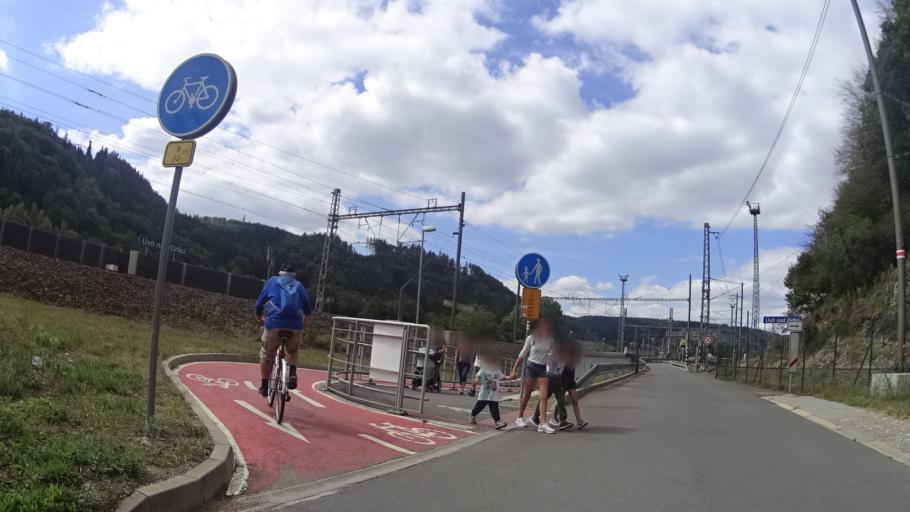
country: CZ
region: Pardubicky
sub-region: Okres Usti nad Orlici
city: Usti nad Orlici
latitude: 49.9716
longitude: 16.3838
